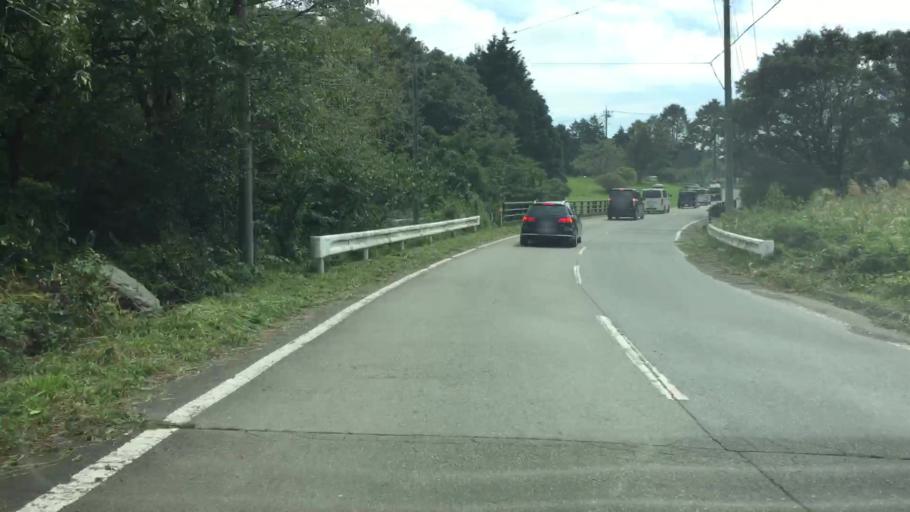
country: JP
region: Yamanashi
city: Fujikawaguchiko
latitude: 35.3948
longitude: 138.5682
